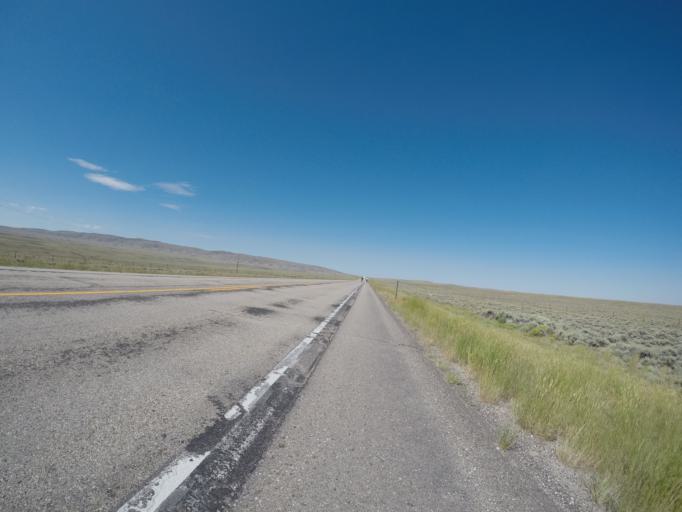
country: US
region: Wyoming
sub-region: Carbon County
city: Saratoga
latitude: 41.8165
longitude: -106.6662
